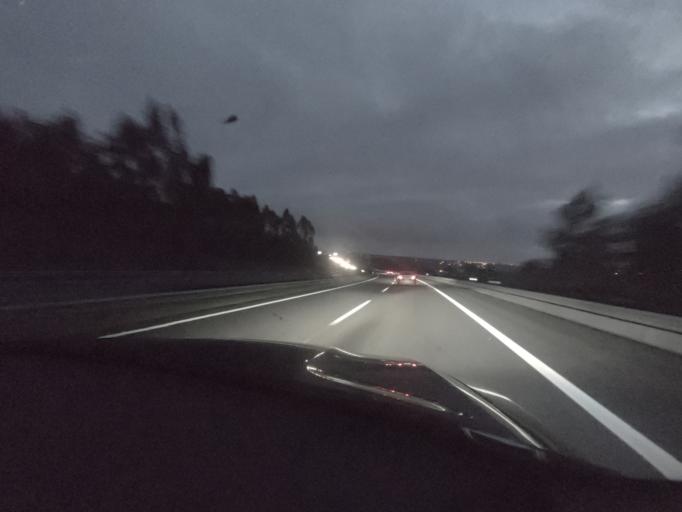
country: PT
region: Leiria
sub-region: Leiria
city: Caranguejeira
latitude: 39.7747
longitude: -8.7433
